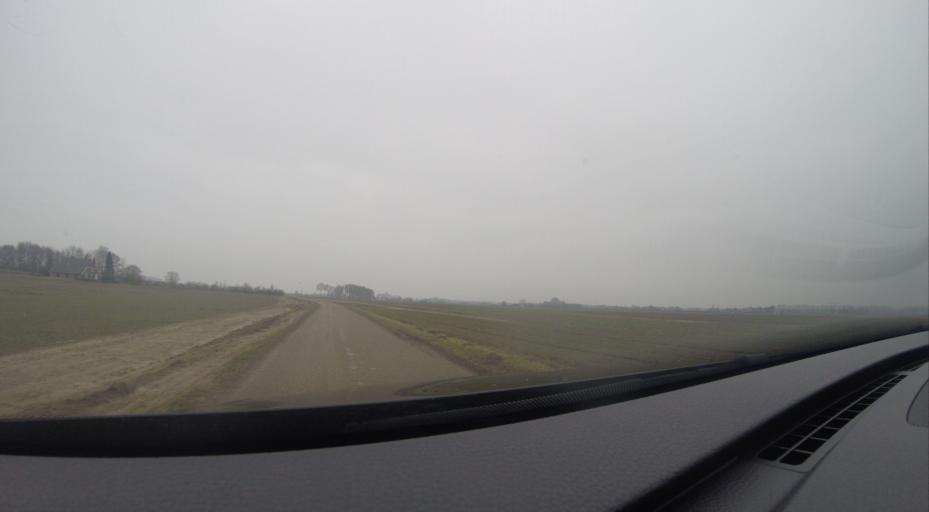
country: NL
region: Gelderland
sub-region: Gemeente Bronckhorst
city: Baak
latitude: 52.0993
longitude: 6.1985
